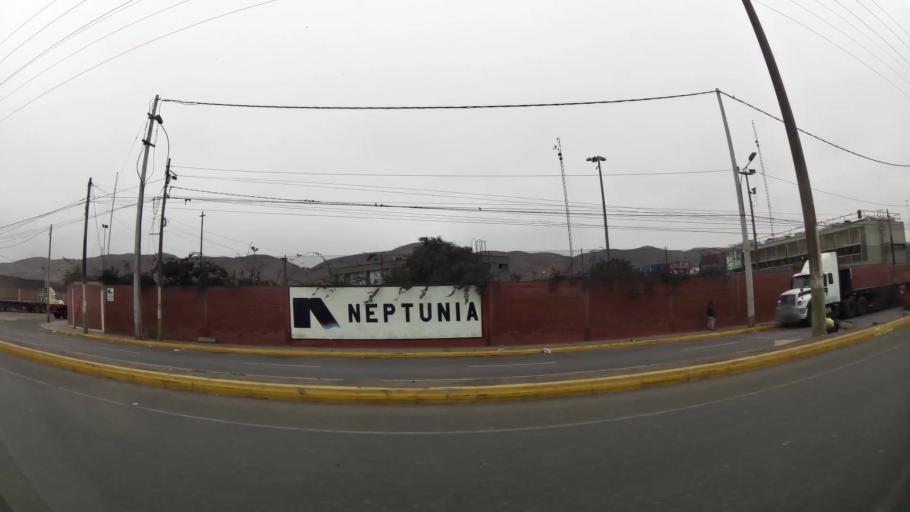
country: PE
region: Lima
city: Ventanilla
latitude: -11.9516
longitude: -77.1308
